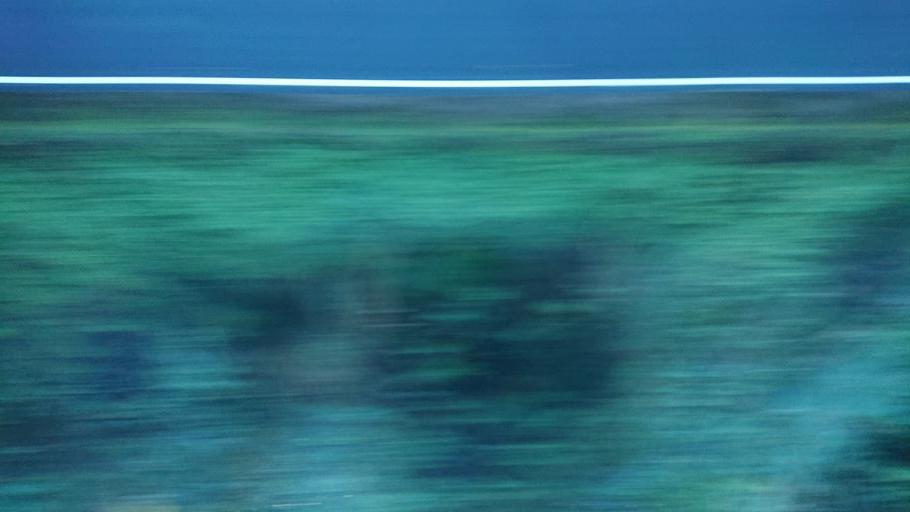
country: TW
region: Taiwan
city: Lugu
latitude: 23.4989
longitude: 120.8192
